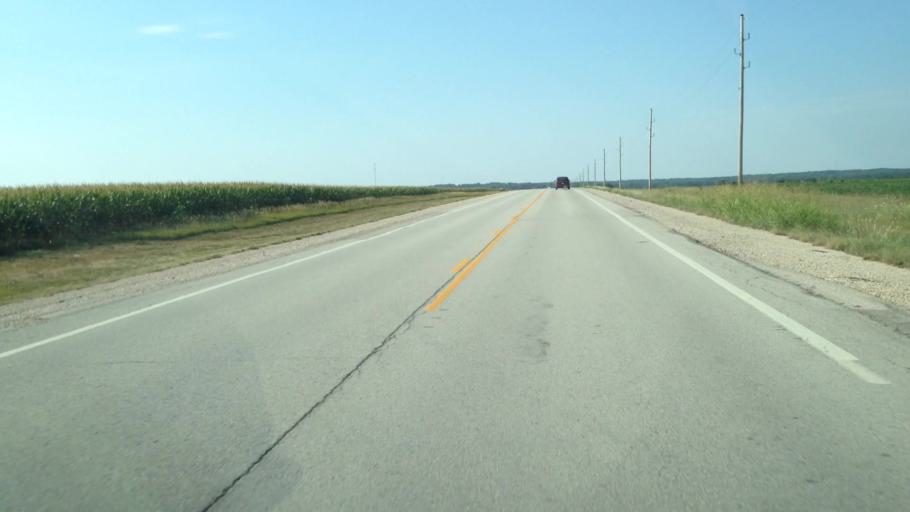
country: US
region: Kansas
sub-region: Anderson County
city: Garnett
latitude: 38.0524
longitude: -95.1695
